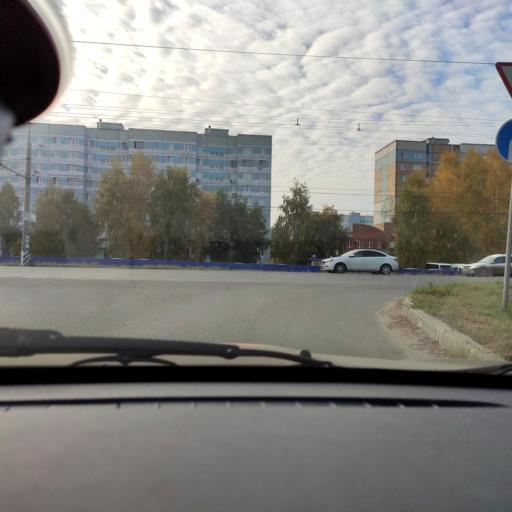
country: RU
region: Samara
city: Tol'yatti
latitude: 53.5473
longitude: 49.3594
